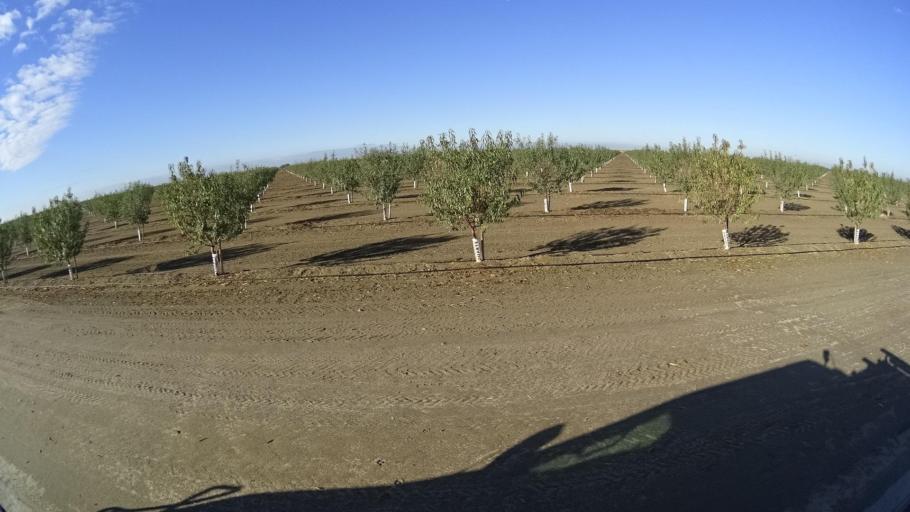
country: US
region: California
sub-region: Kern County
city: Delano
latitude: 35.7151
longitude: -119.2945
